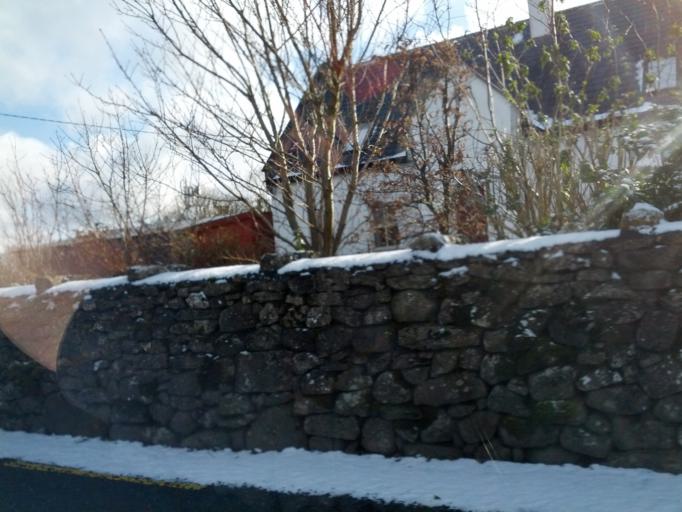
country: IE
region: Connaught
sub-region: County Galway
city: Gort
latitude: 53.1572
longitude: -8.8078
